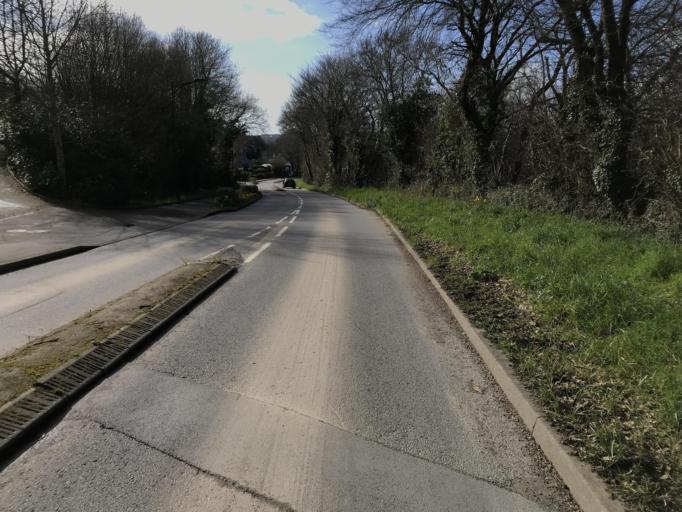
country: FR
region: Brittany
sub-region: Departement du Finistere
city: Loperhet
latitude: 48.3782
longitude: -4.3136
